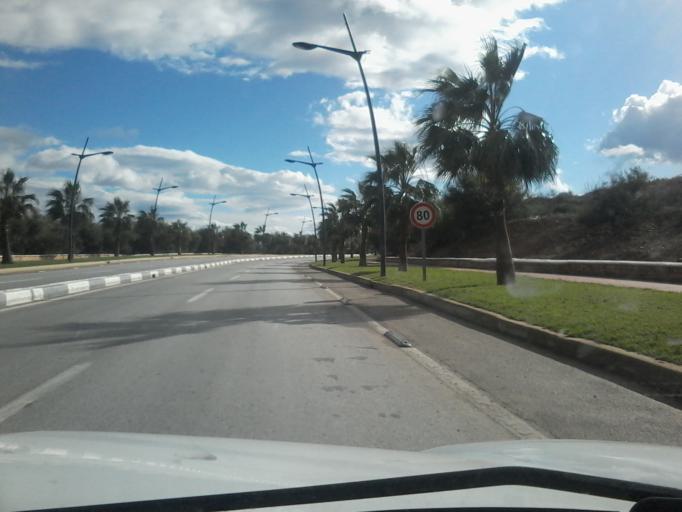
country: ES
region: Ceuta
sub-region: Ceuta
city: Ceuta
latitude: 35.7858
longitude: -5.3521
